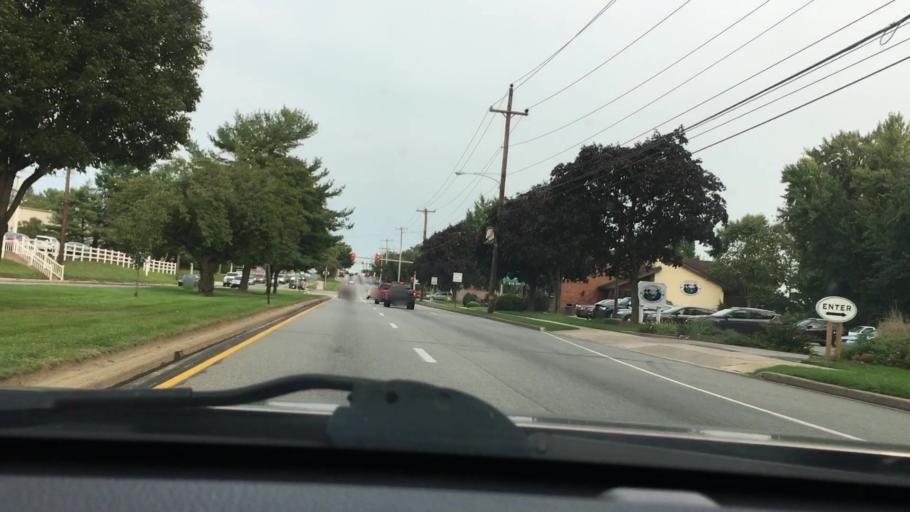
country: US
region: Pennsylvania
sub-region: Delaware County
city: Drexel Hill
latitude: 39.9698
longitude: -75.3015
